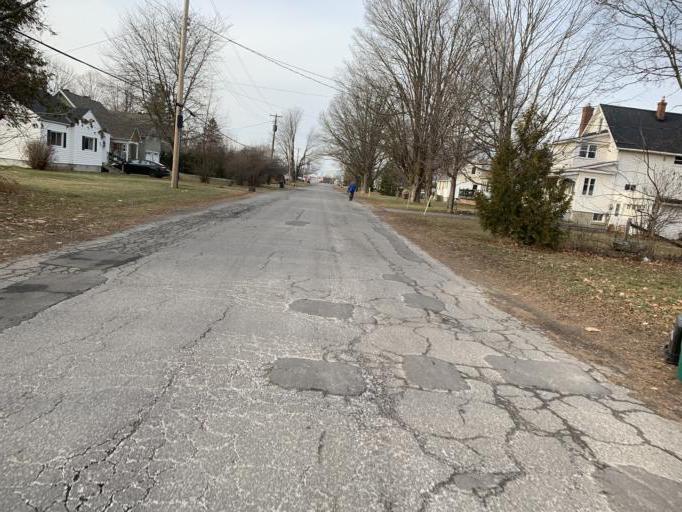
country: CA
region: Ontario
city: Bells Corners
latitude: 45.1930
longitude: -75.8347
